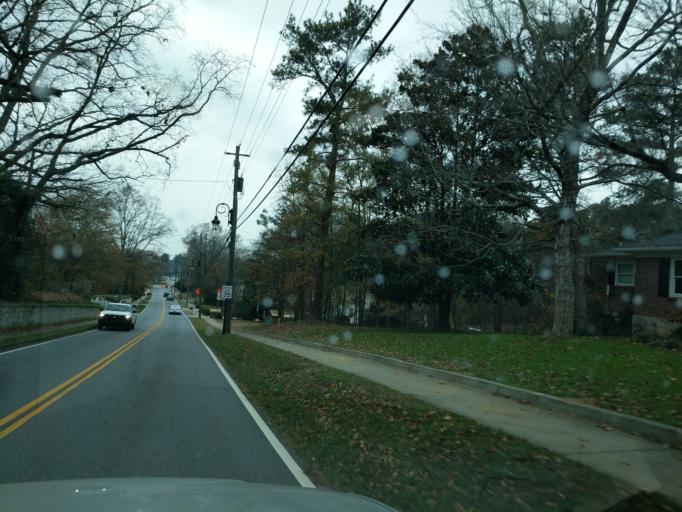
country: US
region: Georgia
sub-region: Gwinnett County
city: Duluth
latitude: 34.0045
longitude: -84.1467
